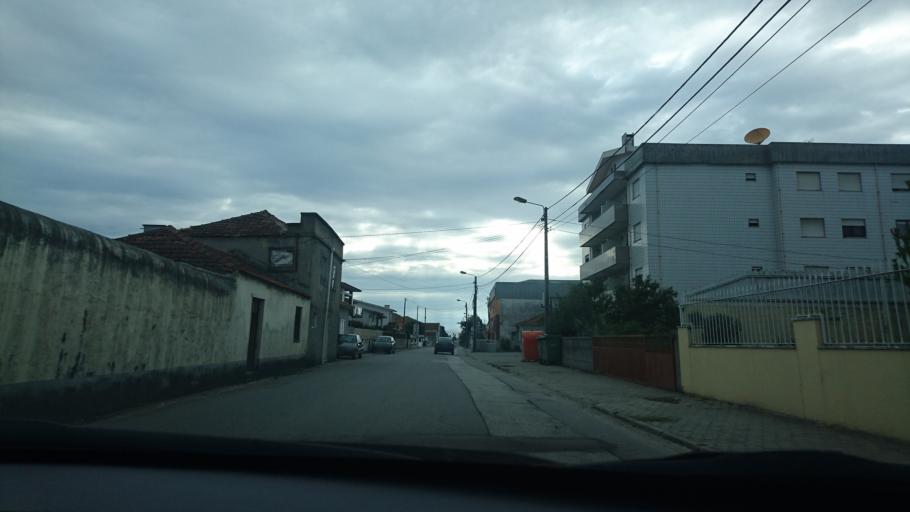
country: PT
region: Aveiro
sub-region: Ovar
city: Cortegaca
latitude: 40.9607
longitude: -8.6020
